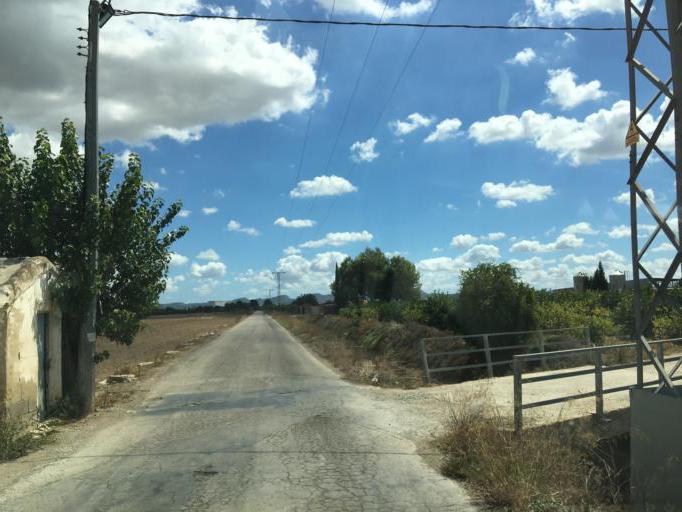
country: ES
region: Murcia
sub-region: Murcia
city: Santomera
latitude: 38.0487
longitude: -1.0480
